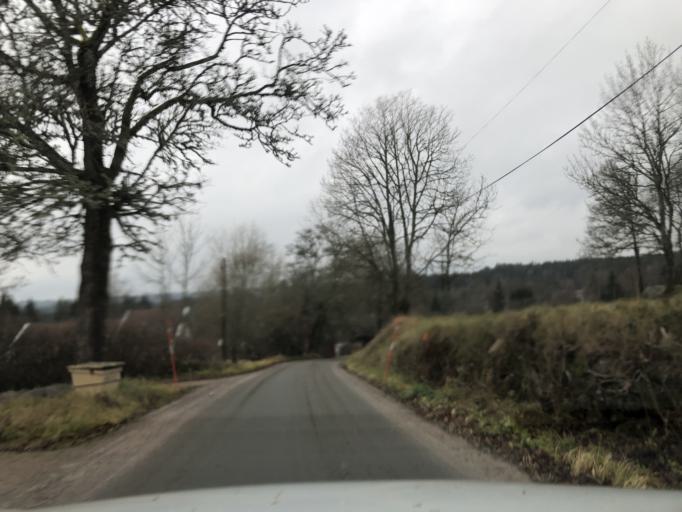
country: SE
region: Vaestra Goetaland
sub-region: Ulricehamns Kommun
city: Ulricehamn
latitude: 57.8611
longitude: 13.5761
